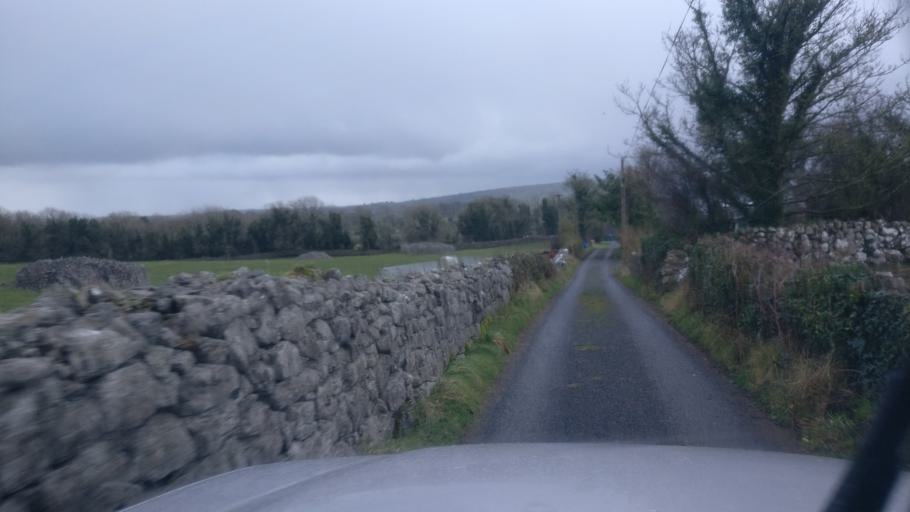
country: IE
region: Connaught
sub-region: County Galway
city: Loughrea
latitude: 53.1919
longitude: -8.6799
